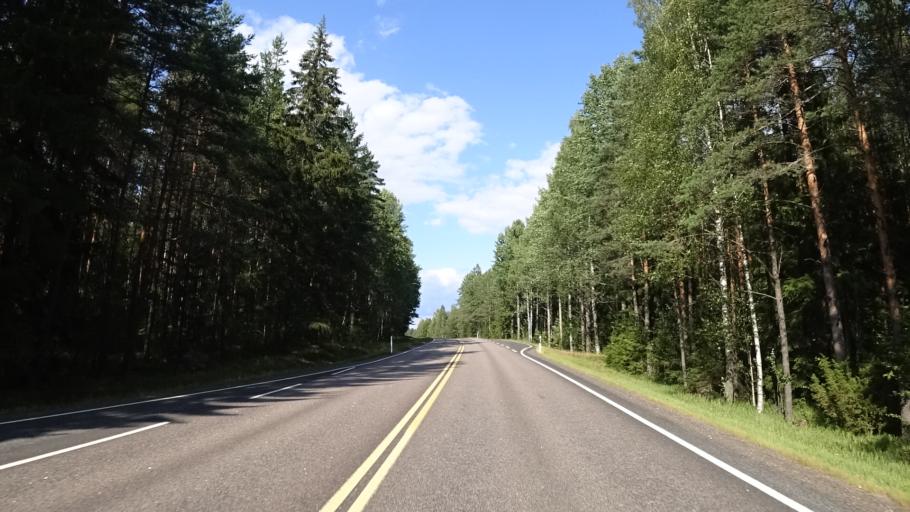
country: FI
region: Kymenlaakso
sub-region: Kotka-Hamina
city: Hamina
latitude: 60.6401
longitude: 27.2337
